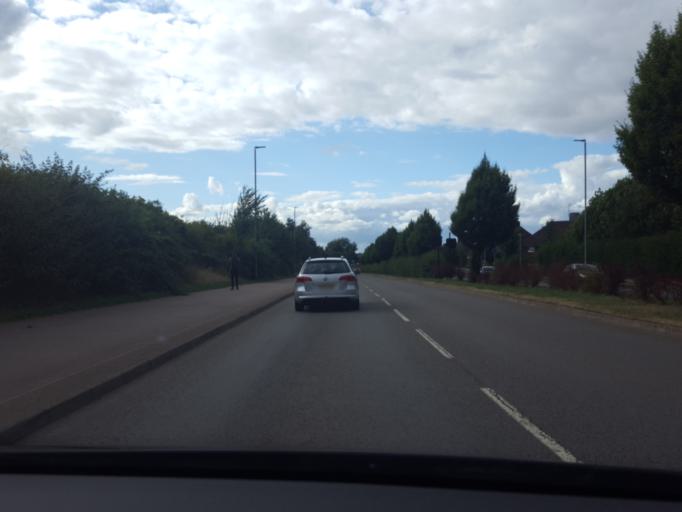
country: GB
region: England
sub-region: Leicestershire
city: Loughborough
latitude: 52.7568
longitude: -1.2018
